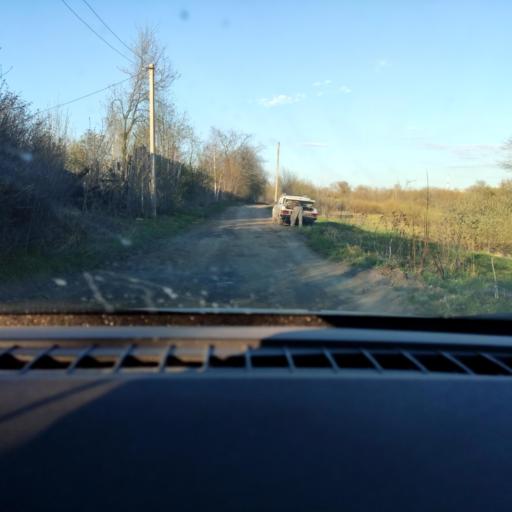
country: RU
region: Perm
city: Perm
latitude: 58.0230
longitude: 56.2044
